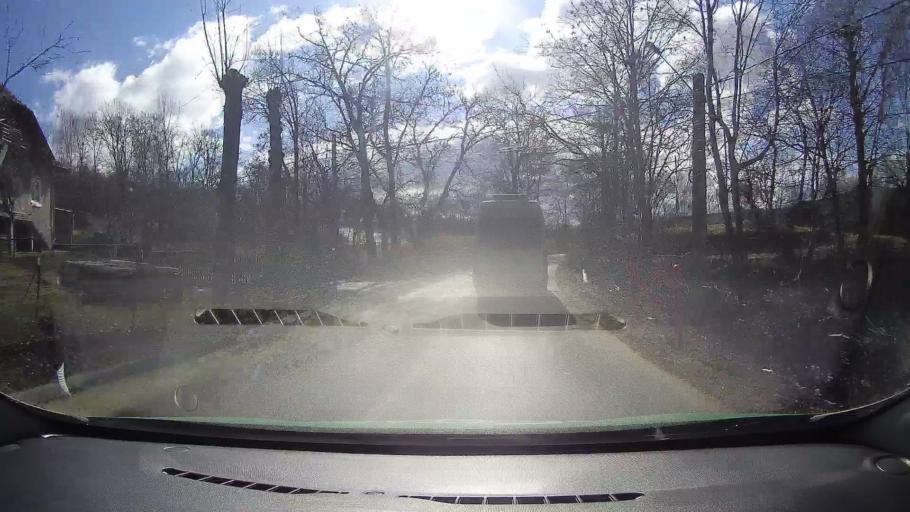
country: RO
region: Dambovita
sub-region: Comuna Runcu
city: Badeni
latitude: 45.1443
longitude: 25.4045
